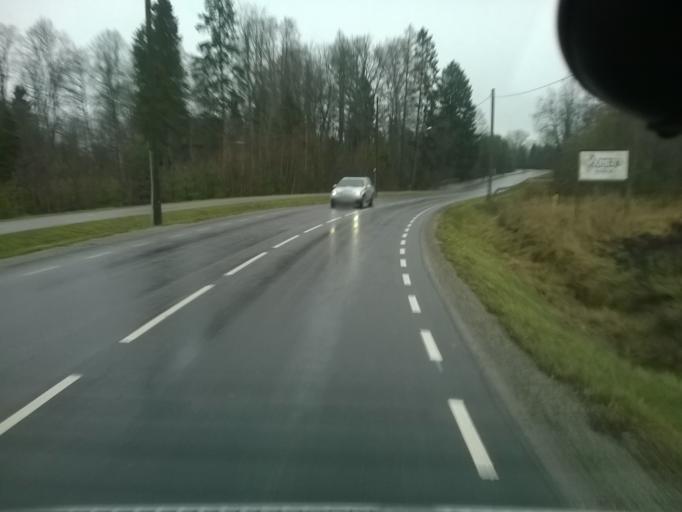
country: EE
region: Harju
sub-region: Saku vald
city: Saku
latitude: 59.2276
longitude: 24.6759
